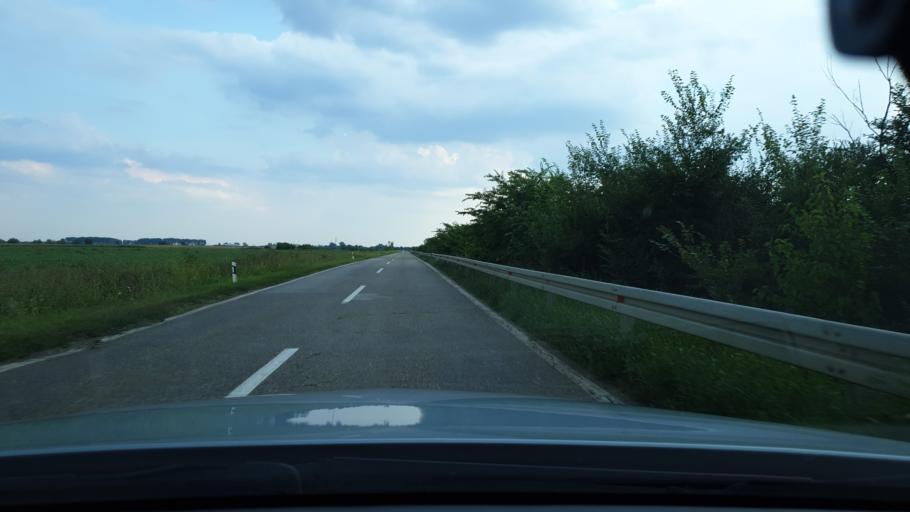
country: RS
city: Stari Lec
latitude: 45.2703
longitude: 20.9493
